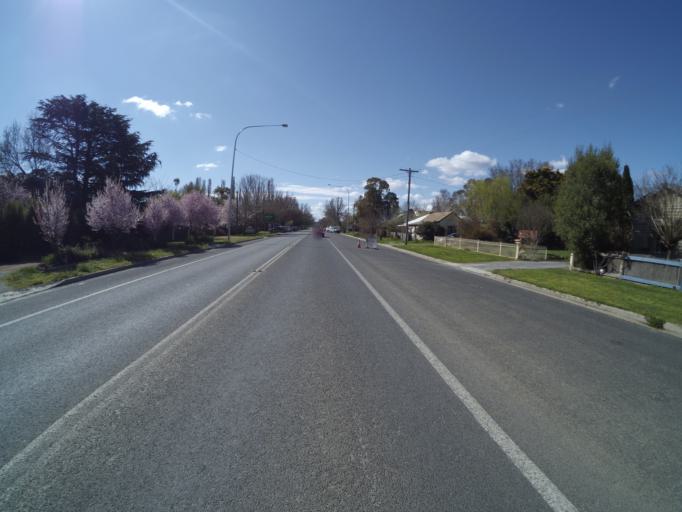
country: AU
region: New South Wales
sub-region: Palerang
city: Bungendore
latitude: -35.2573
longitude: 149.4376
